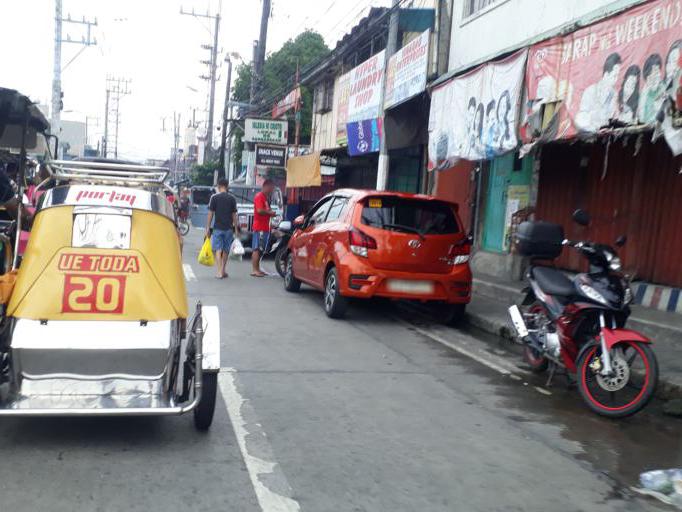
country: PH
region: Metro Manila
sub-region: Caloocan City
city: Niugan
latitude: 14.6600
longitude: 120.9707
